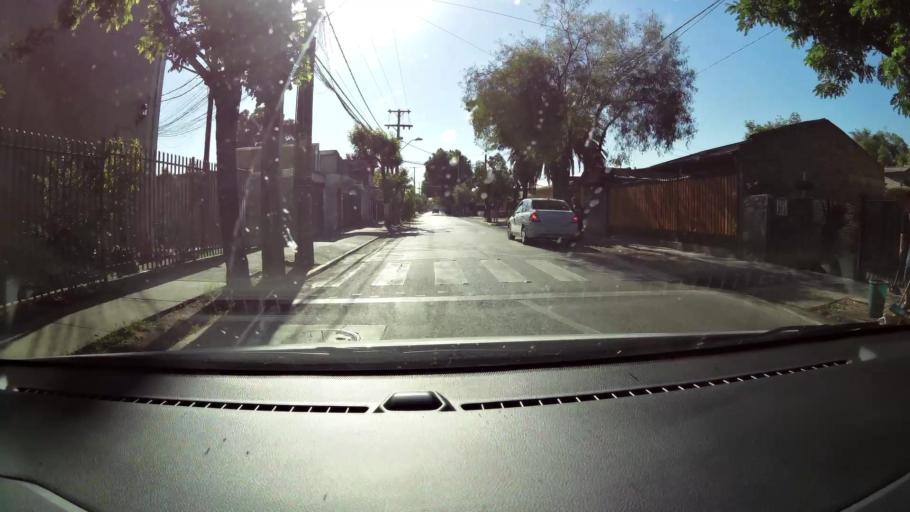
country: CL
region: Santiago Metropolitan
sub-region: Provincia de Maipo
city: San Bernardo
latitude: -33.5499
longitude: -70.6795
